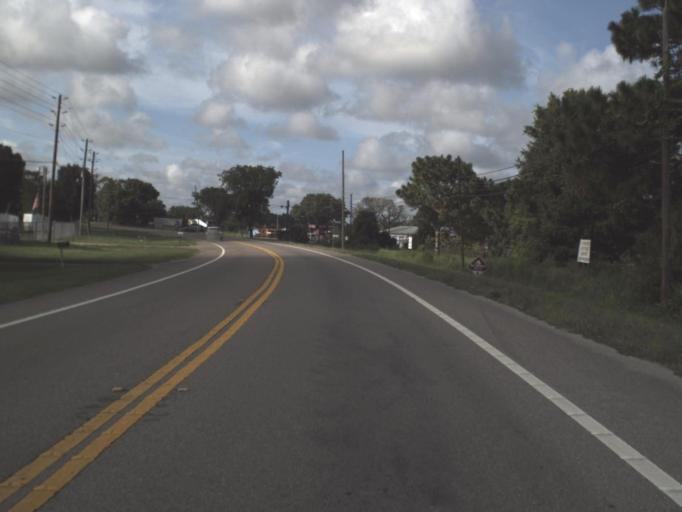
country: US
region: Florida
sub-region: Pasco County
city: Shady Hills
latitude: 28.3152
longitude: -82.5057
